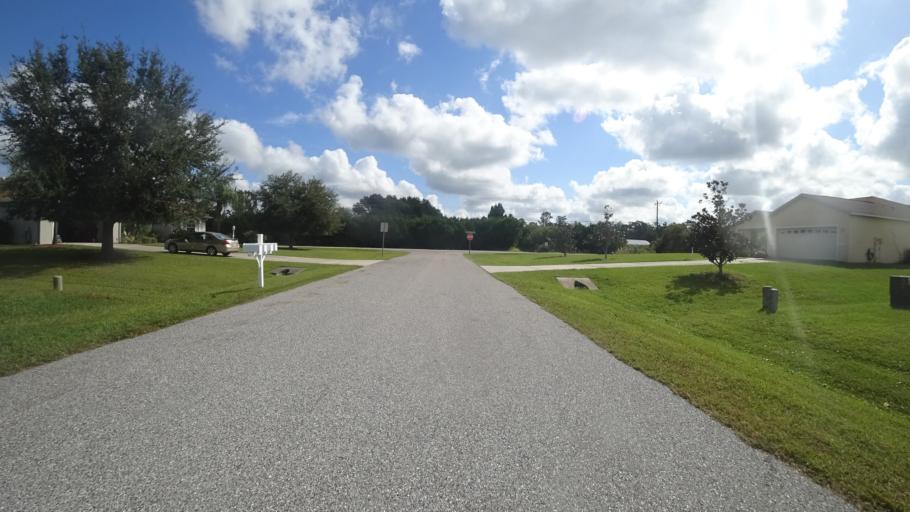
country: US
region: Florida
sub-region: Sarasota County
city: Lake Sarasota
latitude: 27.3921
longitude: -82.2718
